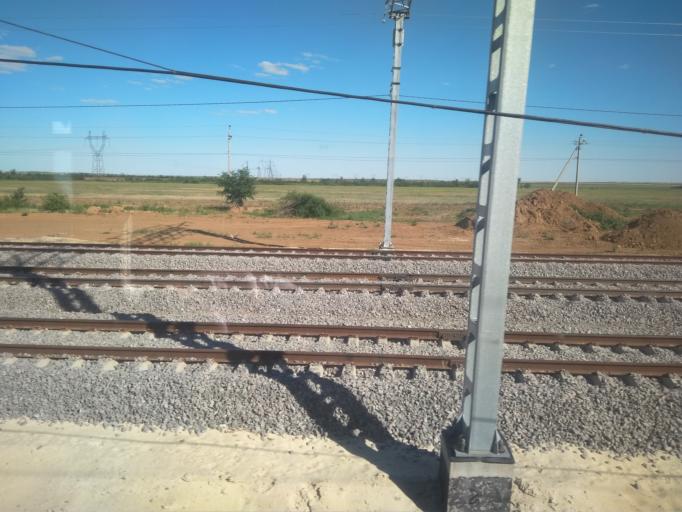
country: RU
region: Volgograd
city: Bereslavka
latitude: 48.2921
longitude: 44.2795
